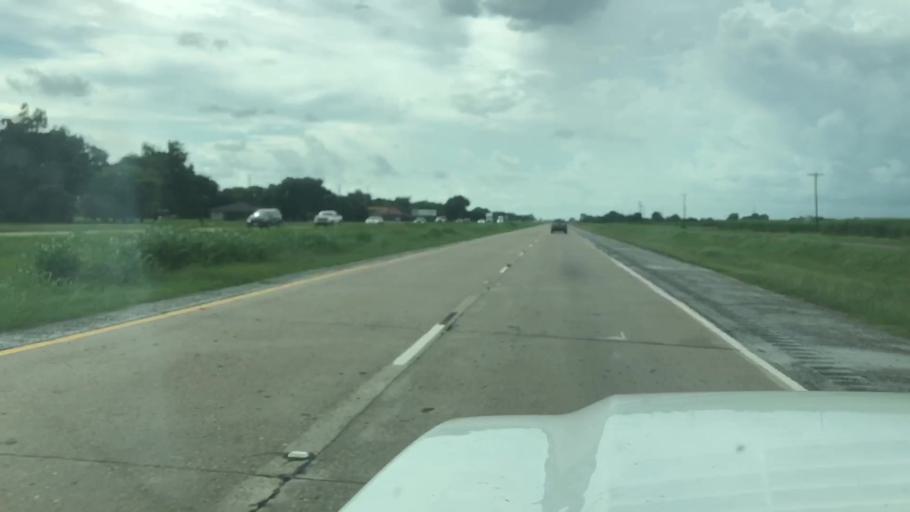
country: US
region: Louisiana
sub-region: Iberia Parish
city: Jeanerette
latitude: 29.8715
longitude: -91.6432
